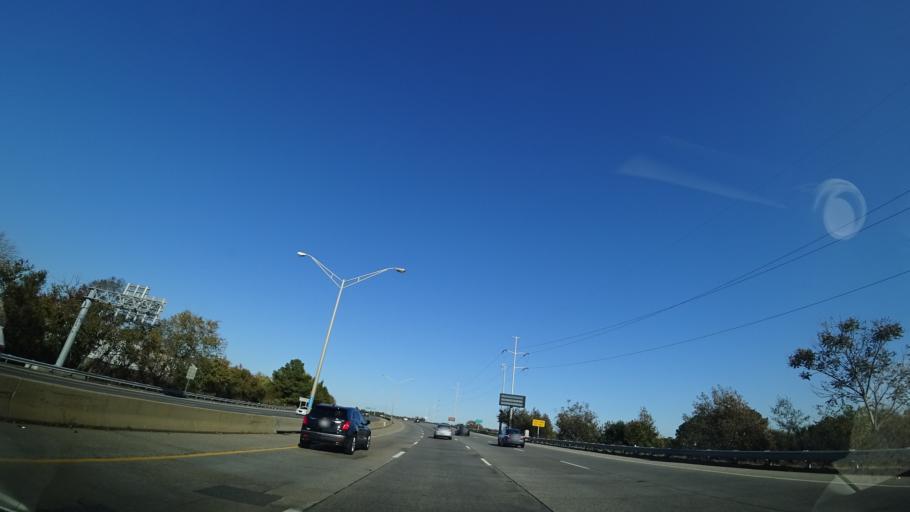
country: US
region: Virginia
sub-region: City of Newport News
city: Newport News
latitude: 36.9980
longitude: -76.4092
